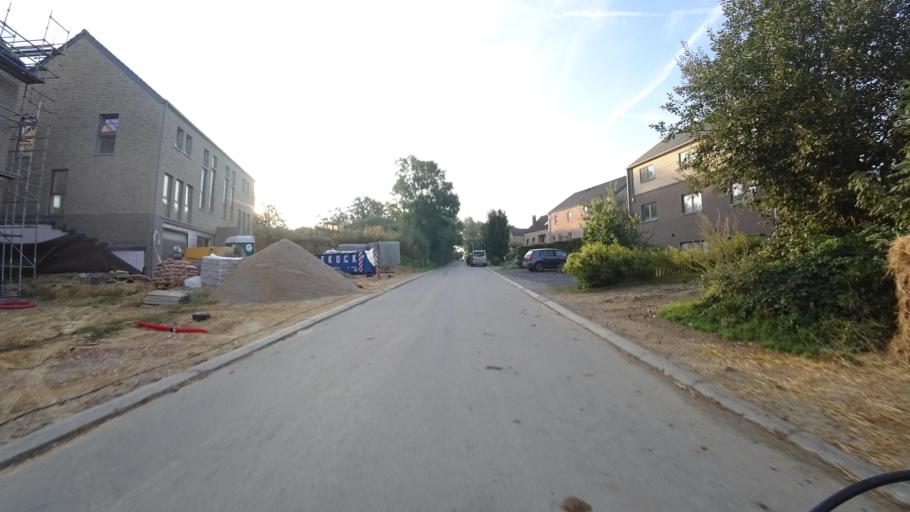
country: BE
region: Wallonia
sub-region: Province du Brabant Wallon
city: Walhain-Saint-Paul
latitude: 50.6198
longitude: 4.6975
